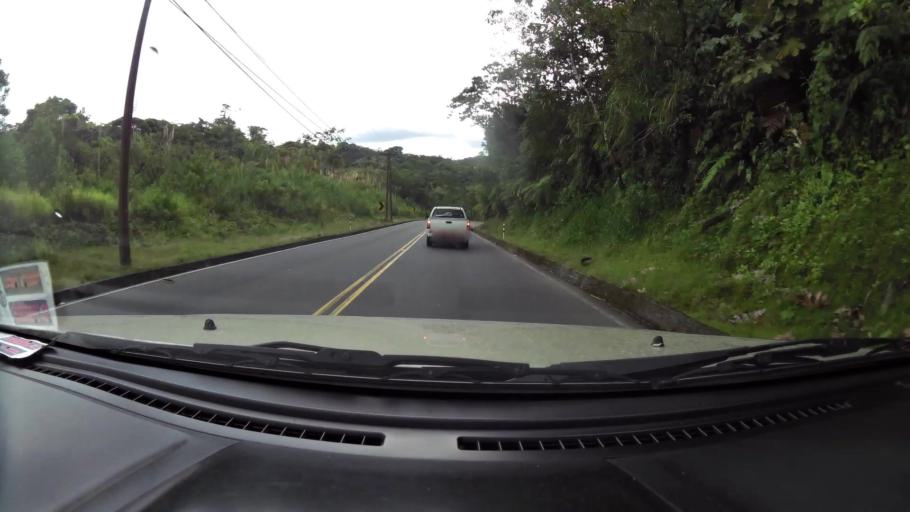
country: EC
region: Pastaza
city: Puyo
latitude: -1.4652
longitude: -78.1066
